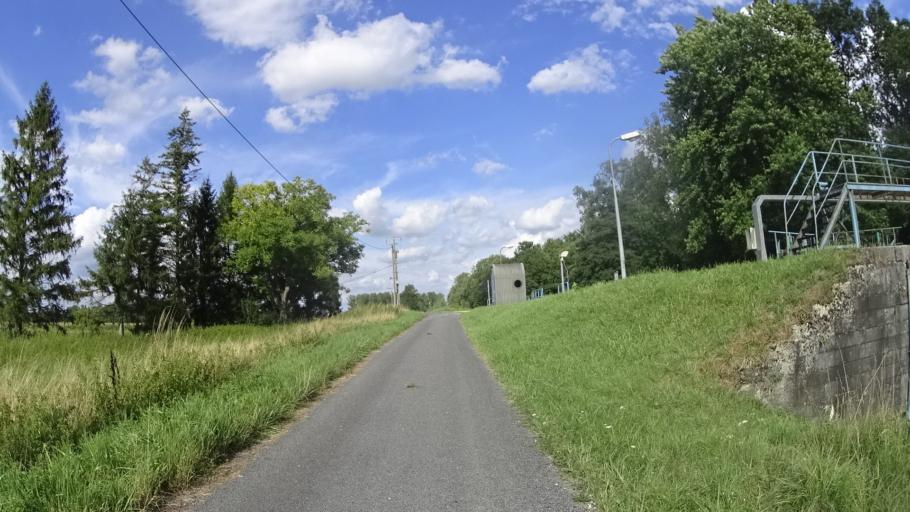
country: FR
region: Champagne-Ardenne
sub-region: Departement de la Marne
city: Pargny-sur-Saulx
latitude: 48.7822
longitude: 4.8687
